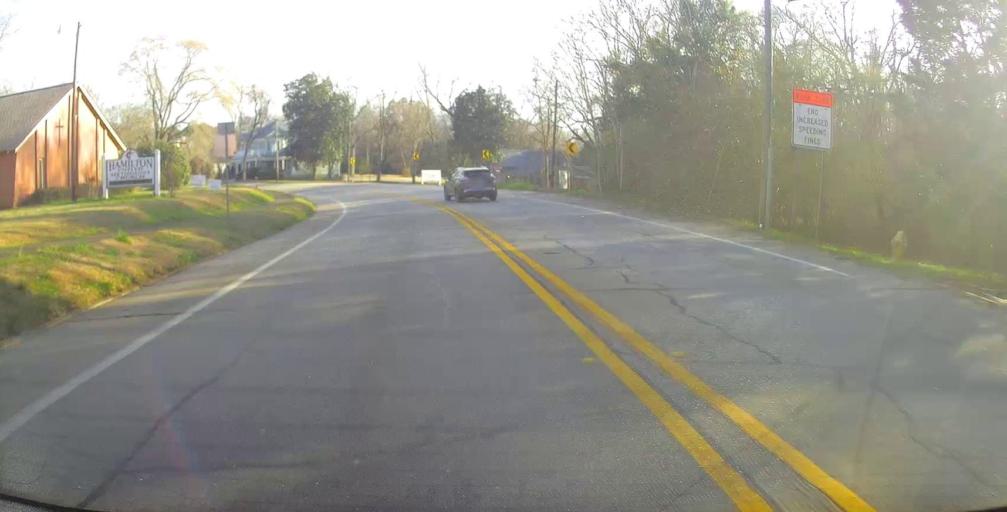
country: US
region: Georgia
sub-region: Harris County
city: Hamilton
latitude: 32.7559
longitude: -84.8751
